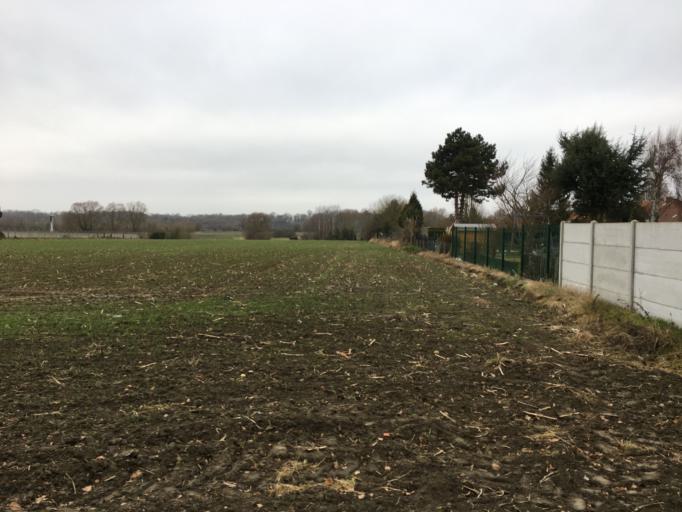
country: FR
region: Nord-Pas-de-Calais
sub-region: Departement du Nord
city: Masny
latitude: 50.3511
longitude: 3.2008
